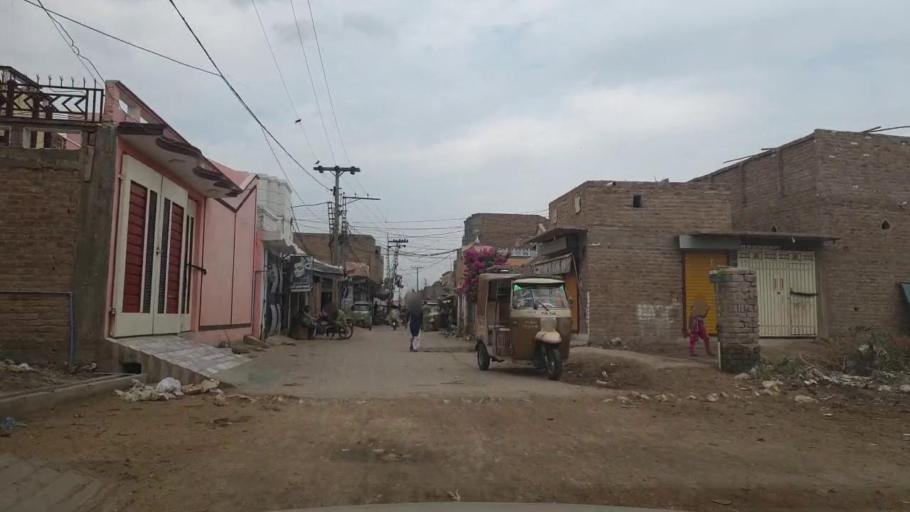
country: PK
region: Sindh
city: Khairpur
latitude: 27.5425
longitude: 68.7406
